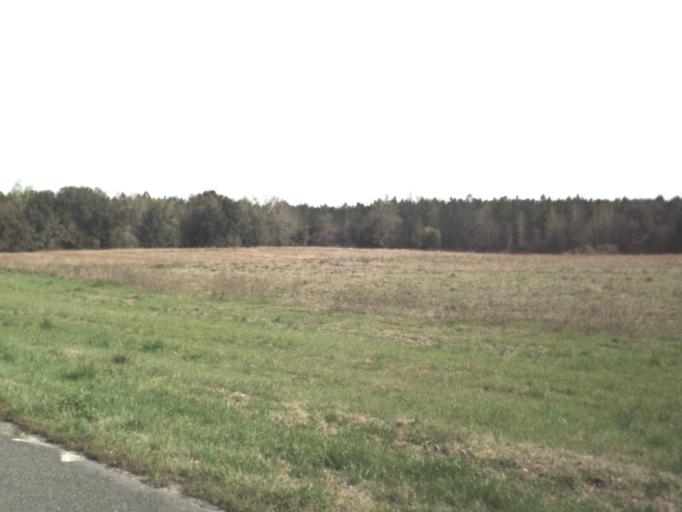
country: US
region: Florida
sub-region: Jefferson County
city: Monticello
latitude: 30.5303
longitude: -83.8209
